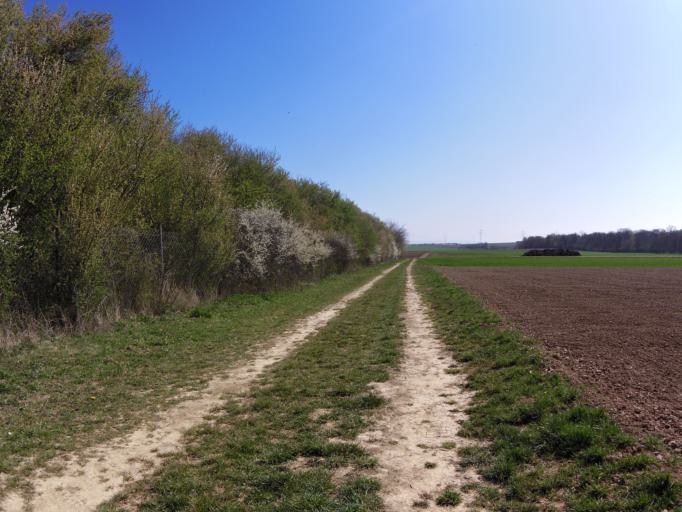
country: DE
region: Bavaria
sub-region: Regierungsbezirk Unterfranken
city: Kurnach
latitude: 49.8375
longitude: 10.0719
